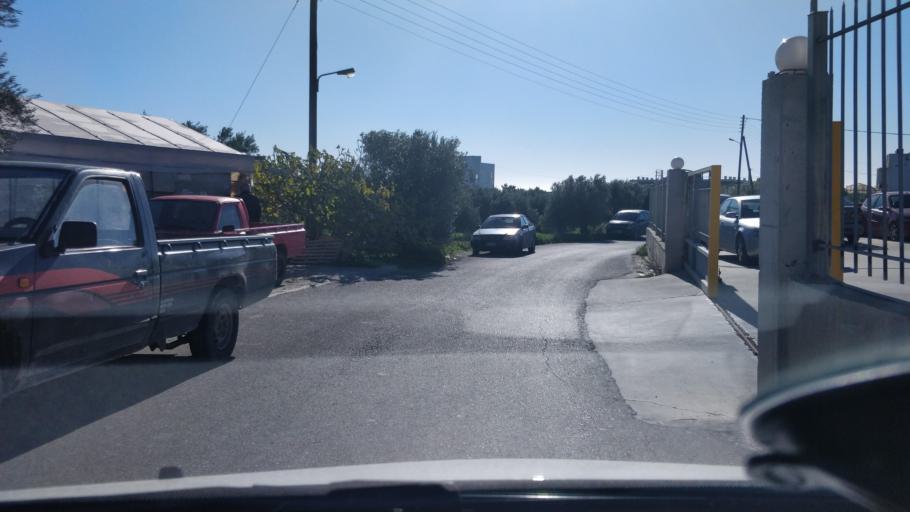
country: GR
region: Crete
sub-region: Nomos Lasithiou
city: Gra Liyia
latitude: 35.0150
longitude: 25.6768
